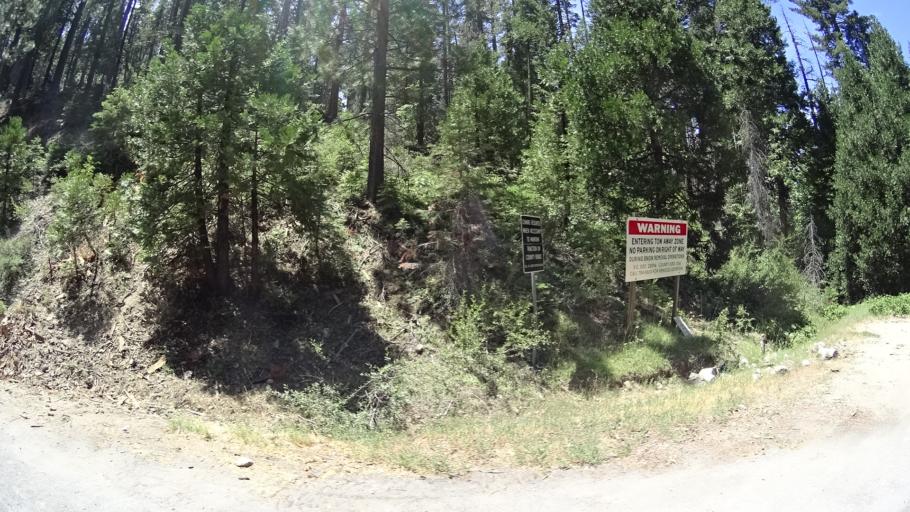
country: US
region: California
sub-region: Calaveras County
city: Arnold
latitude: 38.3139
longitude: -120.2667
